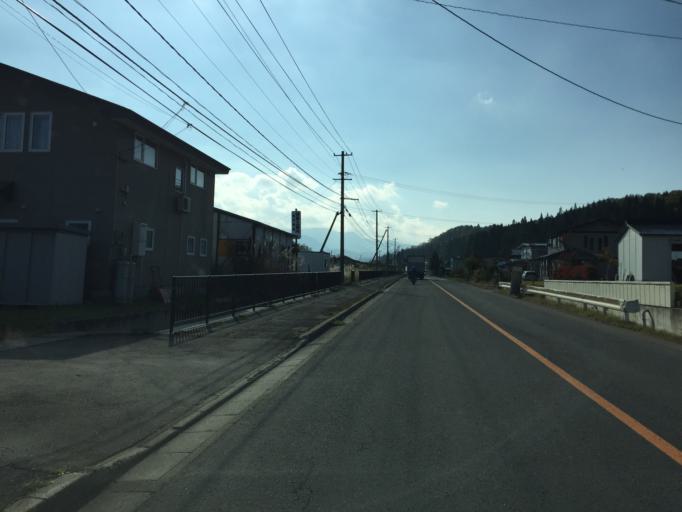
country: JP
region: Yamagata
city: Yonezawa
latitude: 37.9076
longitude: 140.0316
